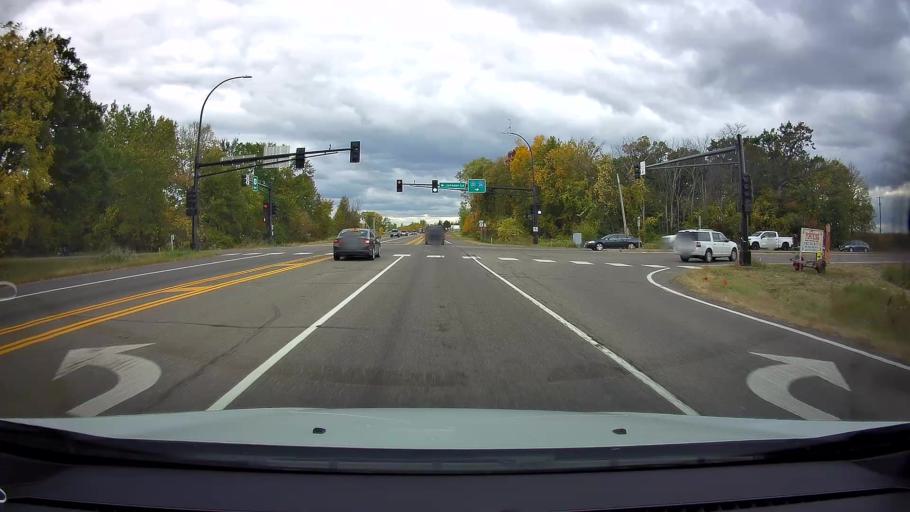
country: US
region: Minnesota
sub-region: Chisago County
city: Chisago City
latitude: 45.3568
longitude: -92.9099
